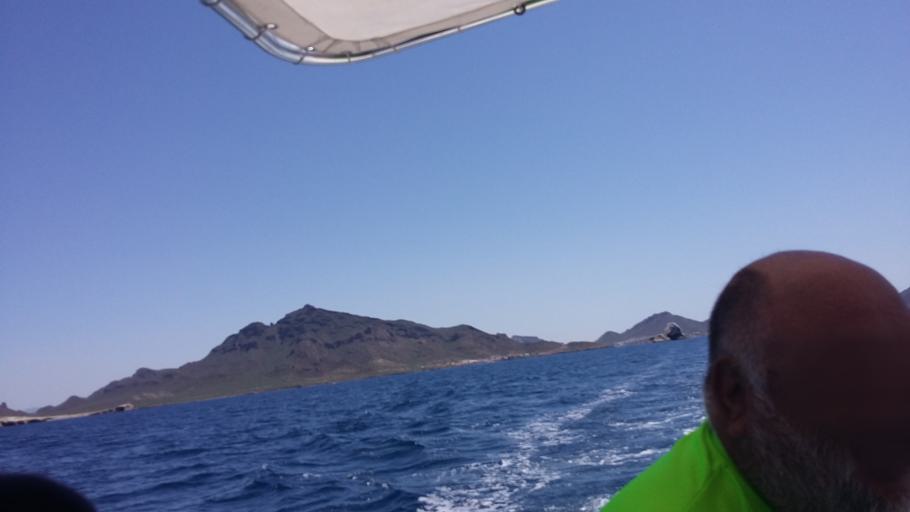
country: MX
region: Sonora
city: Heroica Guaymas
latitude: 27.9268
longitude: -111.0037
